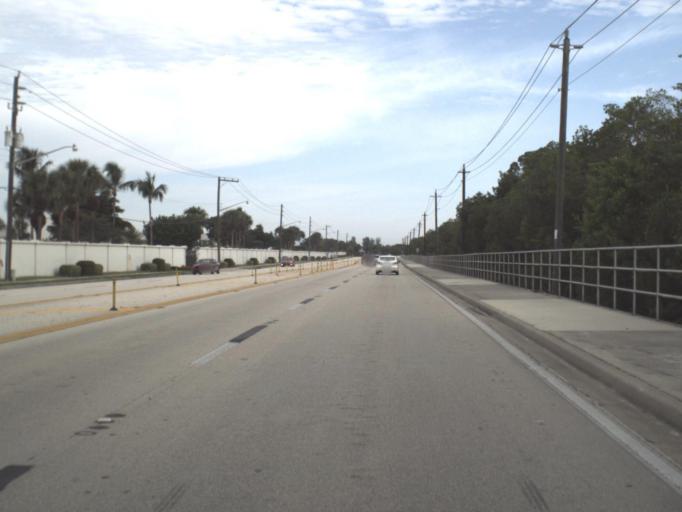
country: US
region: Florida
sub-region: Lee County
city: Fort Myers Beach
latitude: 26.4738
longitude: -81.9511
